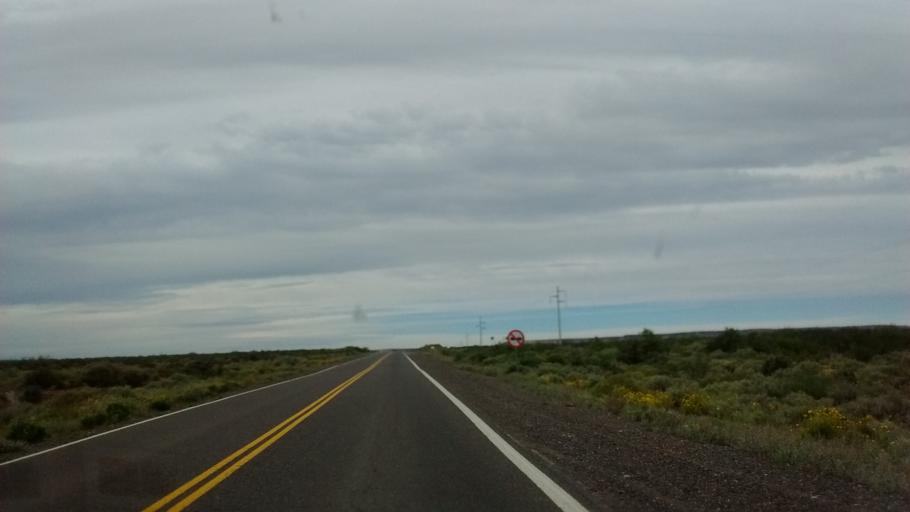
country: AR
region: Rio Negro
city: Catriel
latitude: -38.1520
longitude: -67.9441
